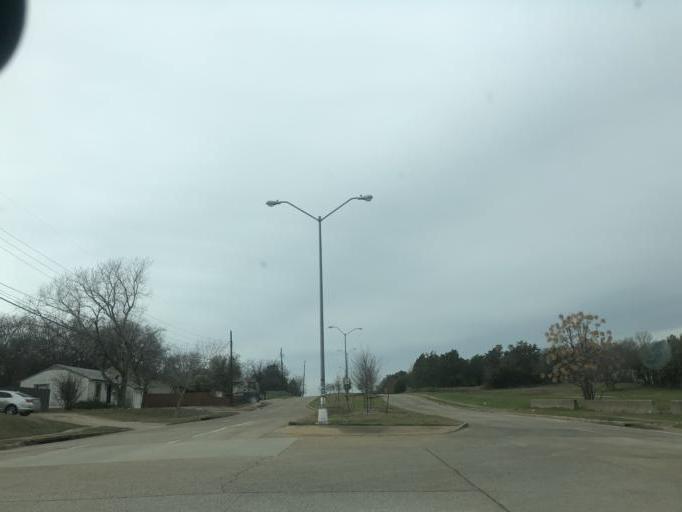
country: US
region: Texas
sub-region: Dallas County
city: Duncanville
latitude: 32.6748
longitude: -96.8291
